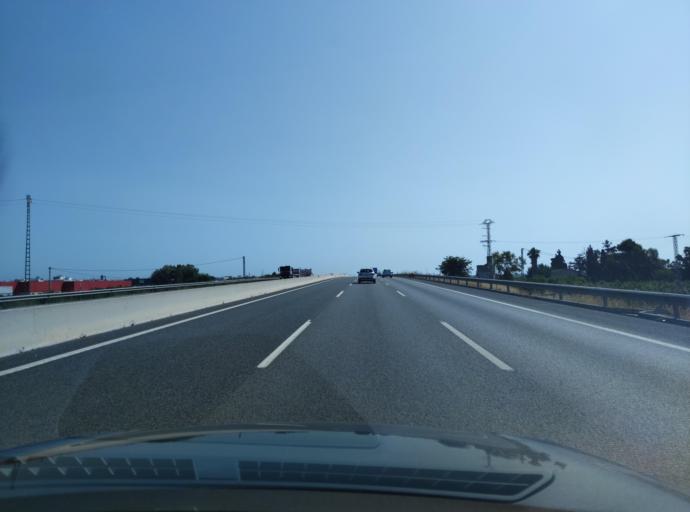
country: ES
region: Valencia
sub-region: Provincia de Valencia
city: L'Alcudia
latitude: 39.1848
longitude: -0.5078
